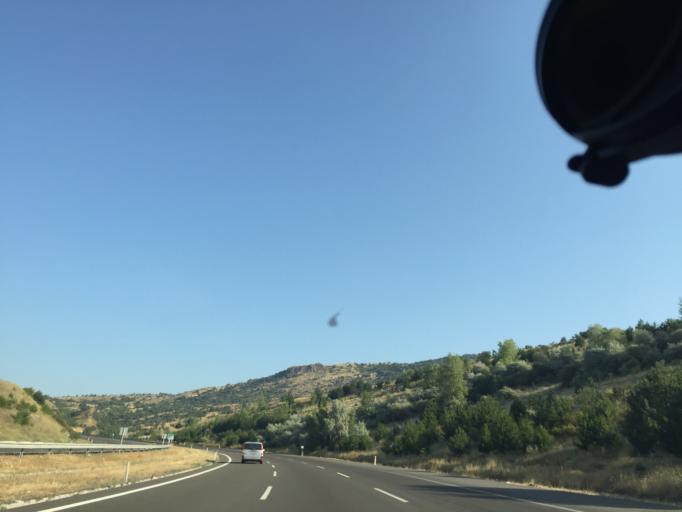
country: TR
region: Ankara
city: Celtikci
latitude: 40.3777
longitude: 32.4705
